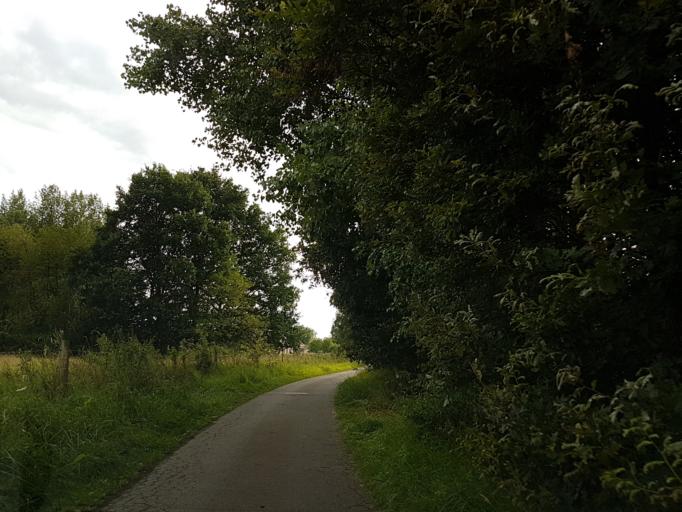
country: BE
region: Flanders
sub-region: Provincie Vlaams-Brabant
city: Kampenhout
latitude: 50.9121
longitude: 4.5846
